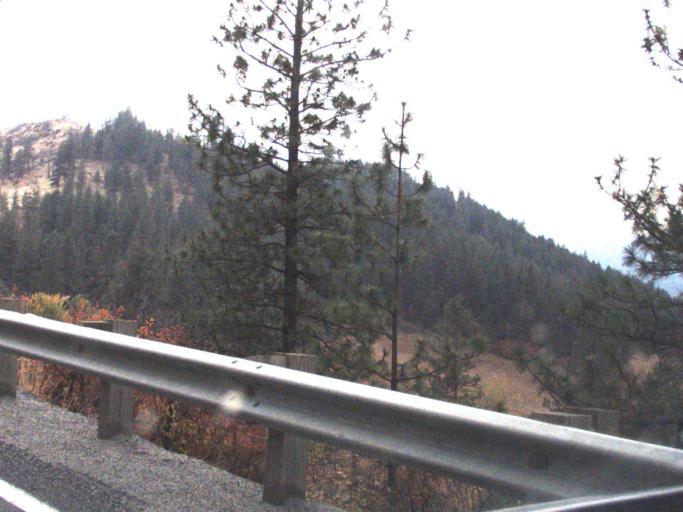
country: US
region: Washington
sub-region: Lincoln County
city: Davenport
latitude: 48.1156
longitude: -118.2012
